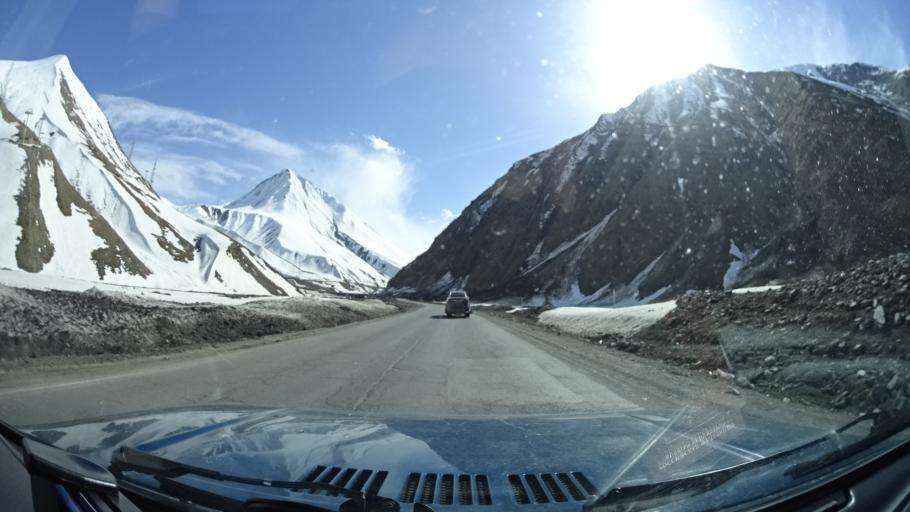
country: GE
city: Gudauri
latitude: 42.5503
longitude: 44.4945
